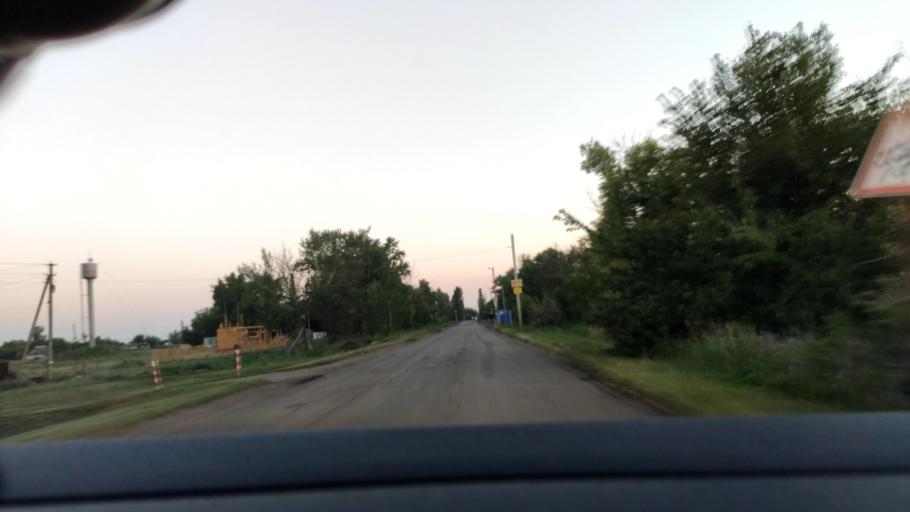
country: RU
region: Voronezj
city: Maslovka
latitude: 51.5122
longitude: 39.2963
